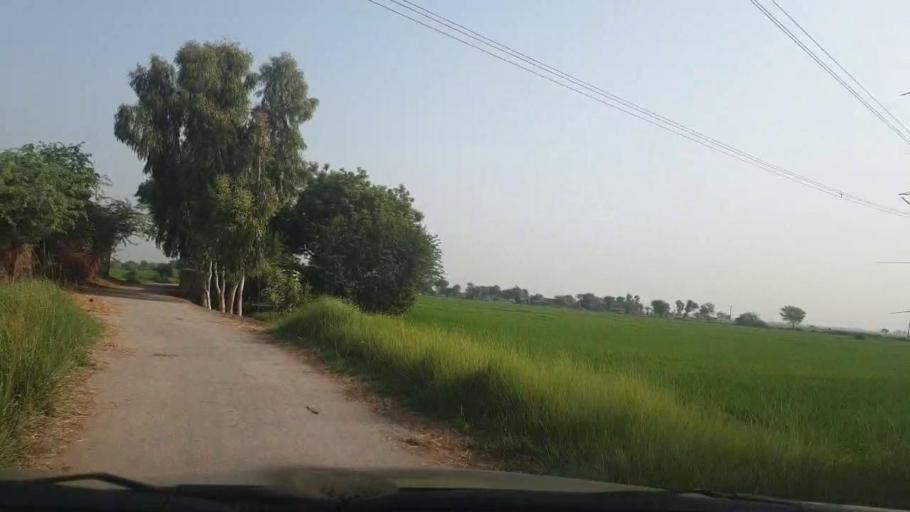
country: PK
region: Sindh
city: Larkana
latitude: 27.5919
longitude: 68.1607
